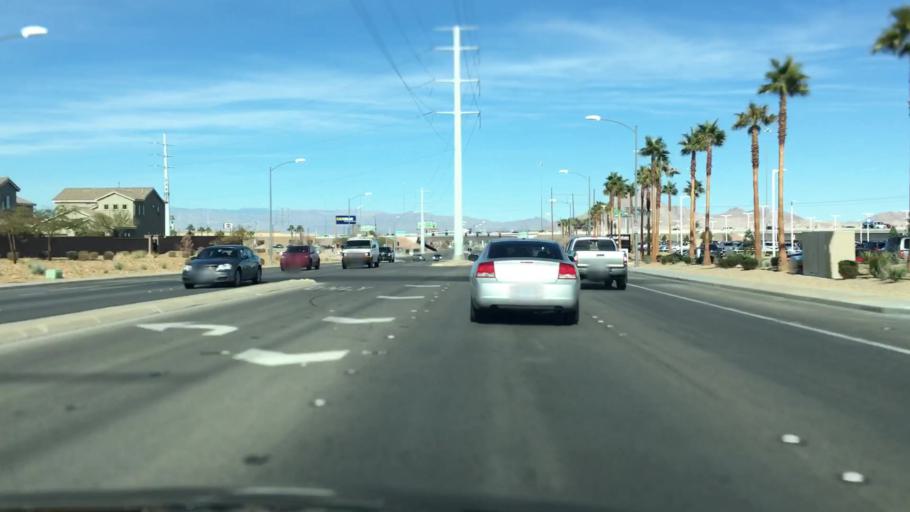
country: US
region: Nevada
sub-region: Clark County
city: Henderson
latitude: 36.0542
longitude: -115.0287
